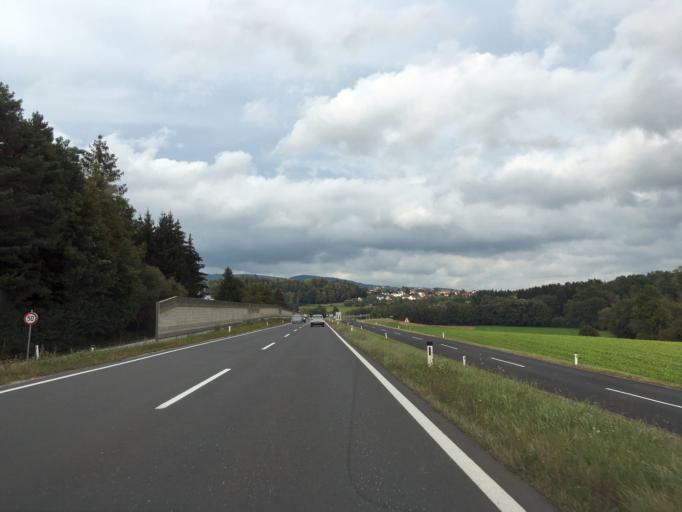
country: AT
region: Styria
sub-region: Politischer Bezirk Hartberg-Fuerstenfeld
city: Dechantskirchen
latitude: 47.4072
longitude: 16.0056
